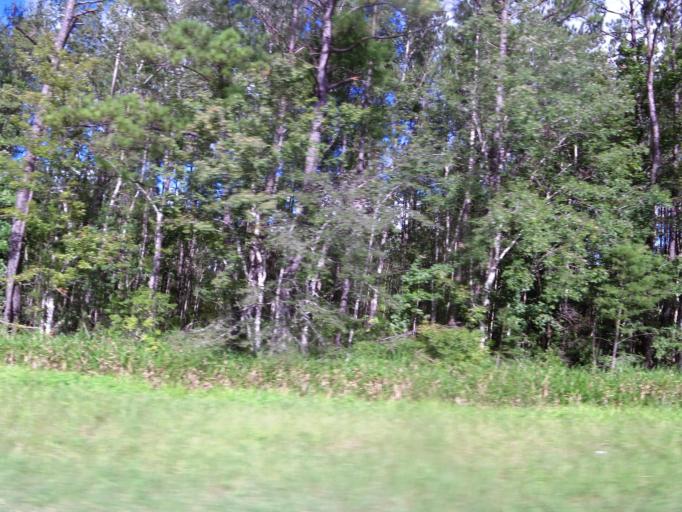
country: US
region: Georgia
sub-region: Camden County
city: Woodbine
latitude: 30.9116
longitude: -81.7121
